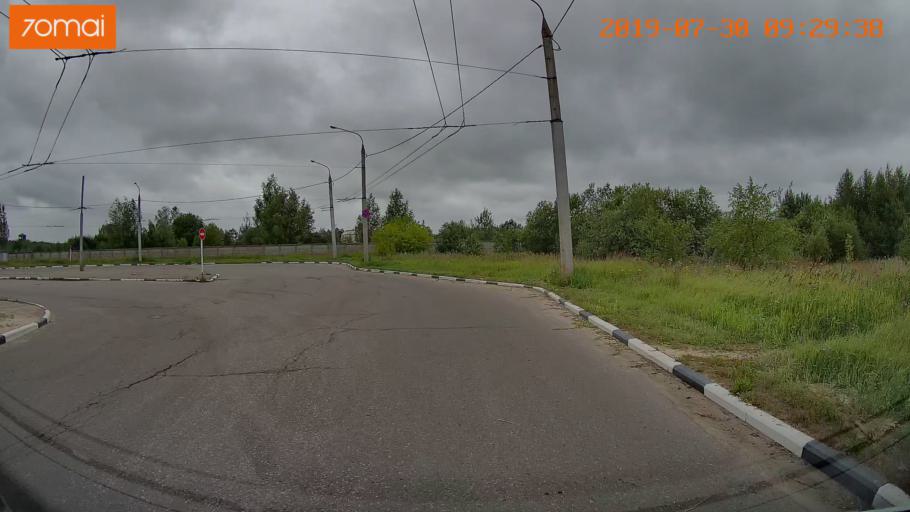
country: RU
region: Ivanovo
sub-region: Gorod Ivanovo
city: Ivanovo
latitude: 56.9435
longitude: 40.9438
